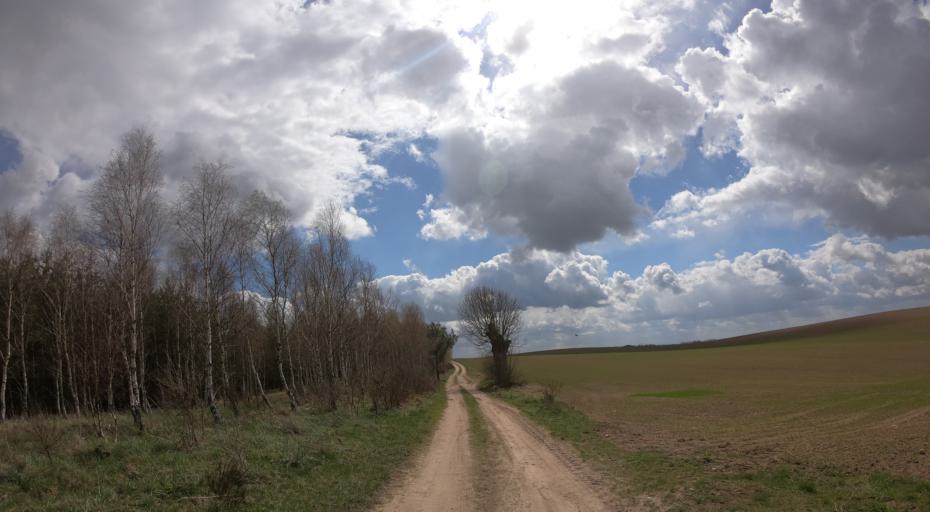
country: PL
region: West Pomeranian Voivodeship
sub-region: Powiat drawski
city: Drawsko Pomorskie
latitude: 53.5553
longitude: 15.8570
